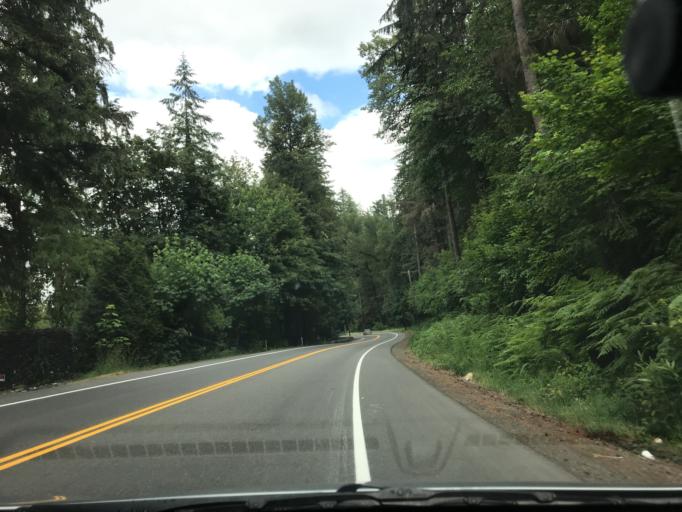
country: US
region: Washington
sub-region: King County
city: Lea Hill
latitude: 47.3163
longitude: -122.1495
